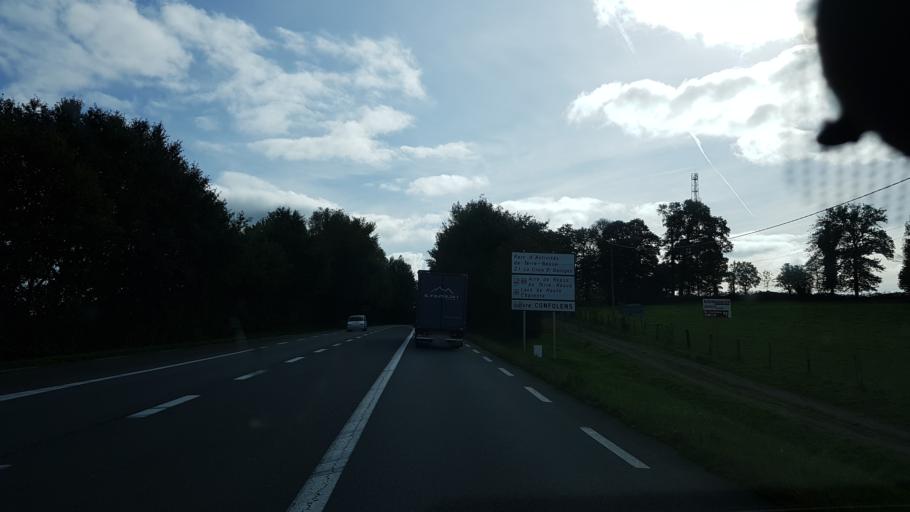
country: FR
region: Poitou-Charentes
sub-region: Departement de la Charente
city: Confolens
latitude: 46.0333
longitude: 0.6588
